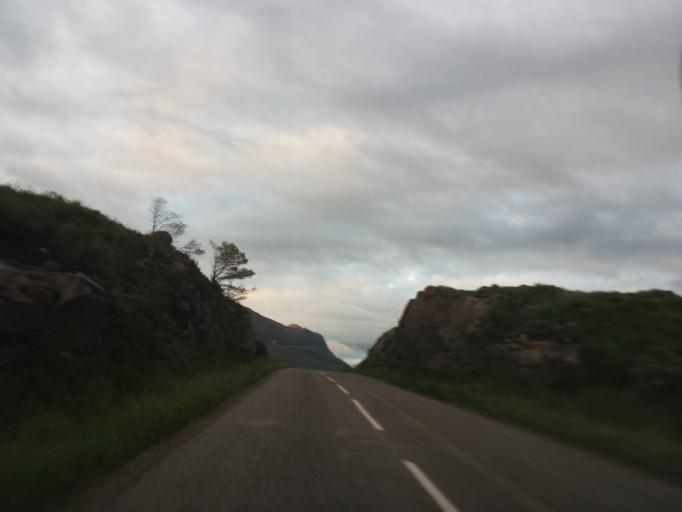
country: GB
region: Scotland
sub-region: Highland
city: Ullapool
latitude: 57.5271
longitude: -5.5679
